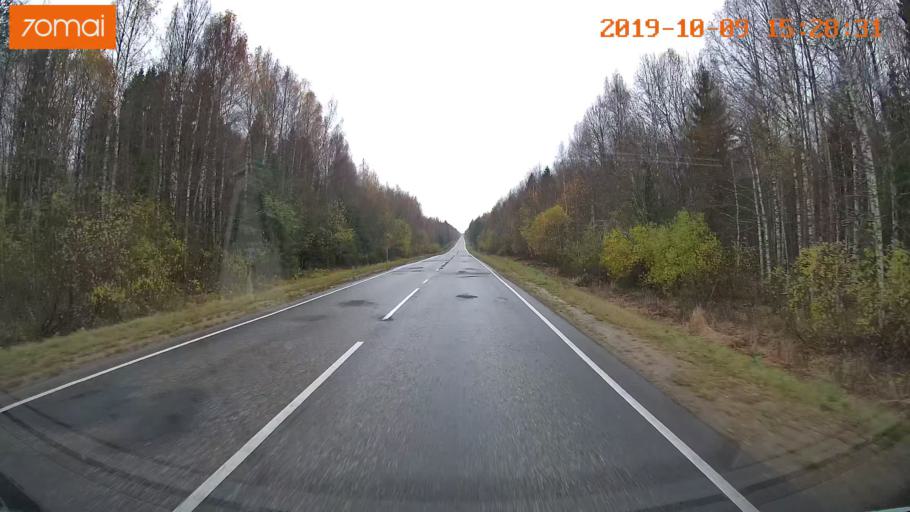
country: RU
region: Kostroma
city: Susanino
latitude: 58.0021
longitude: 41.3585
